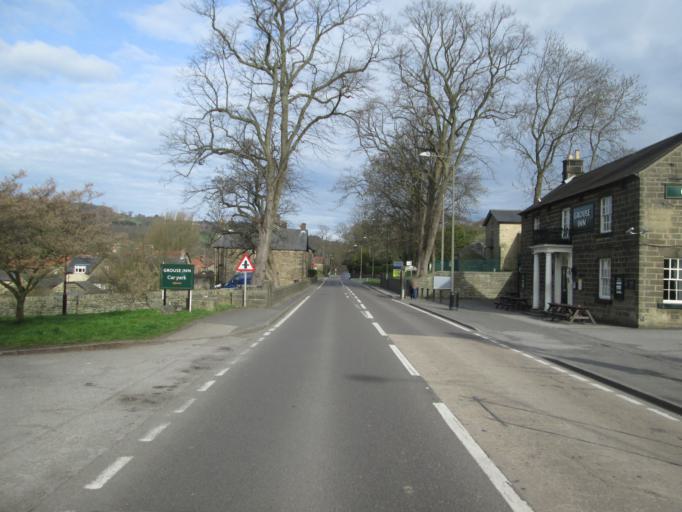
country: GB
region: England
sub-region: Derbyshire
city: Matlock
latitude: 53.1669
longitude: -1.5993
